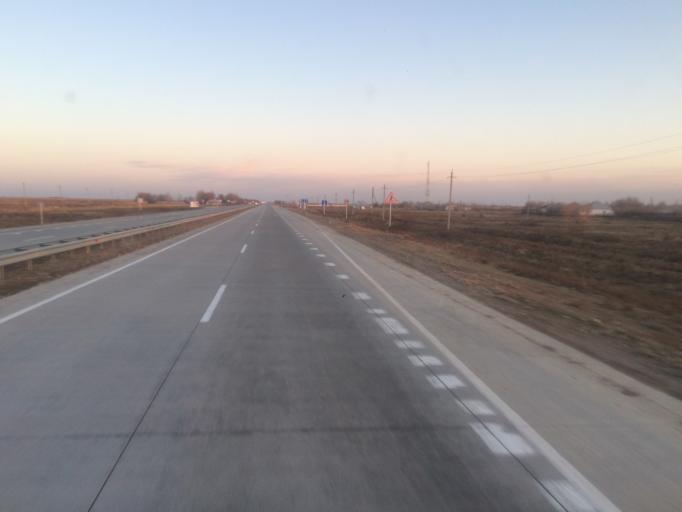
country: KZ
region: Ongtustik Qazaqstan
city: Bayaldyr
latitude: 43.0641
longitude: 68.6777
